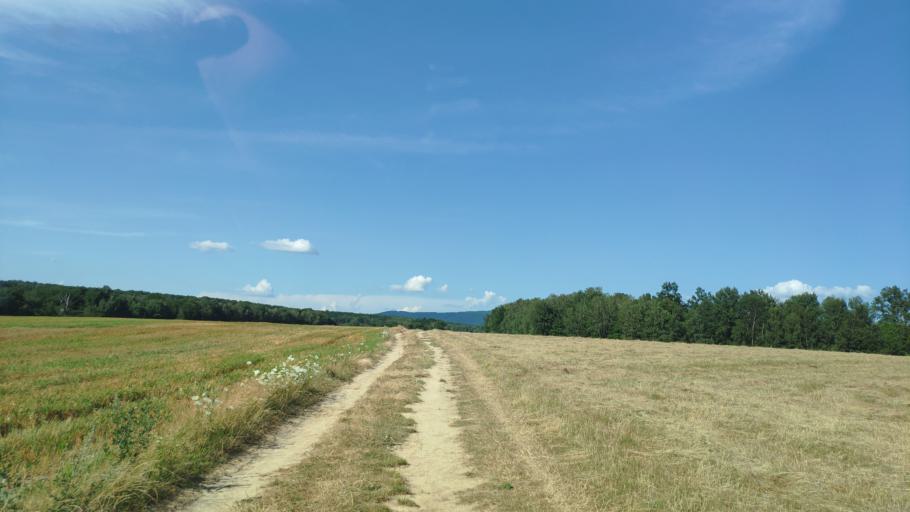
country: SK
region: Presovsky
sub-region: Okres Presov
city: Presov
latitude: 48.9100
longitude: 21.2935
